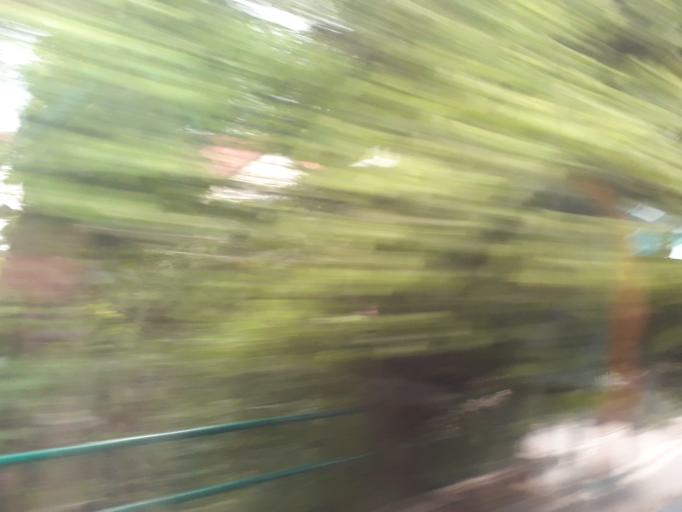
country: MY
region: Perak
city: Ipoh
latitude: 4.6015
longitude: 101.0766
